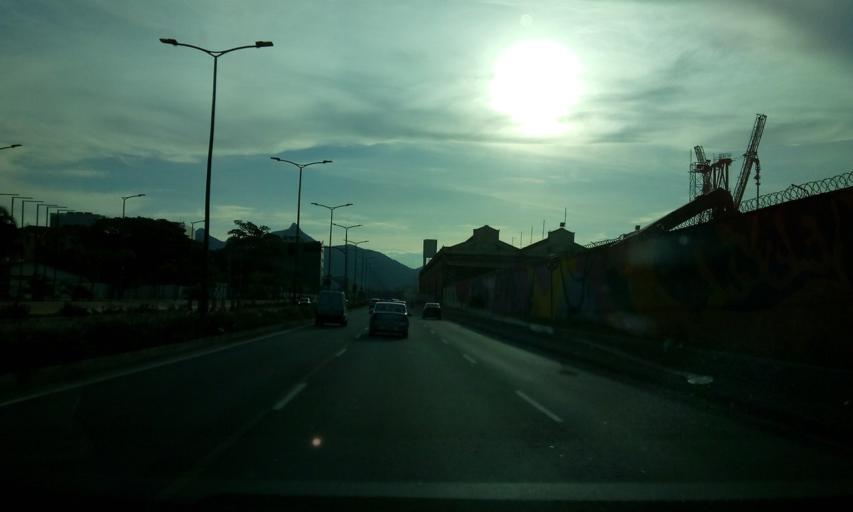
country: BR
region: Rio de Janeiro
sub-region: Rio De Janeiro
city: Rio de Janeiro
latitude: -22.8932
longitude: -43.1973
